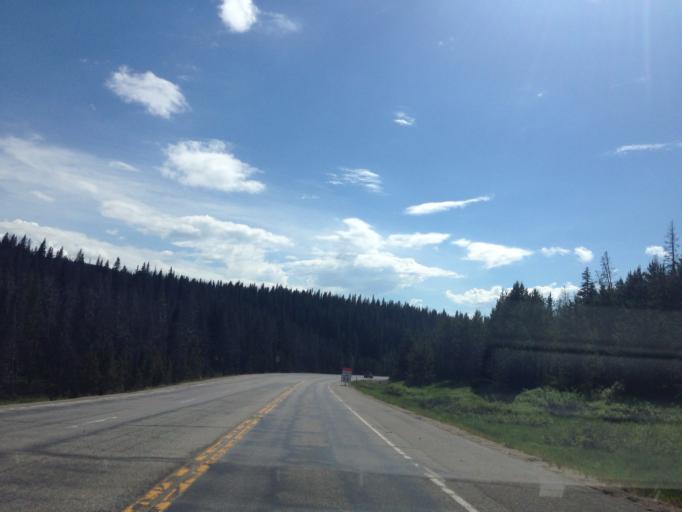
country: US
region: Colorado
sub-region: Routt County
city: Steamboat Springs
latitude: 40.3833
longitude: -106.6853
